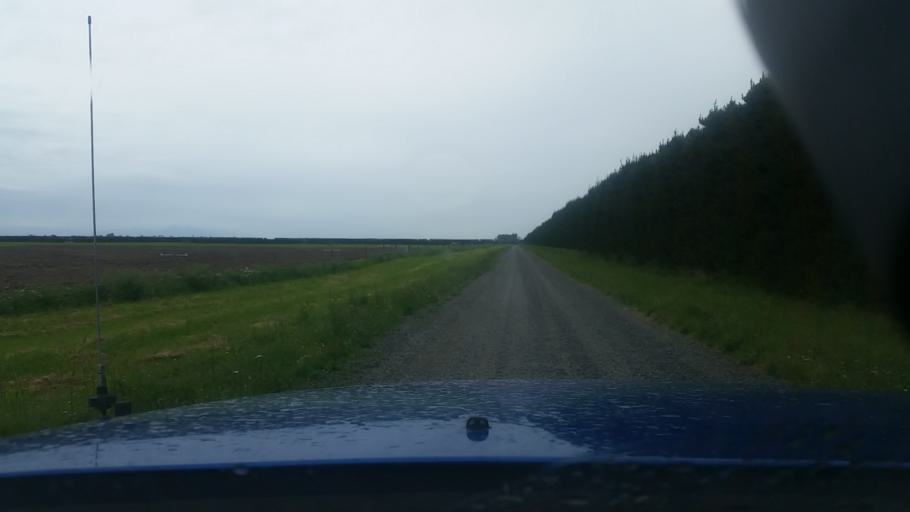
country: NZ
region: Canterbury
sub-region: Ashburton District
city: Rakaia
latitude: -43.9106
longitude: 172.1407
